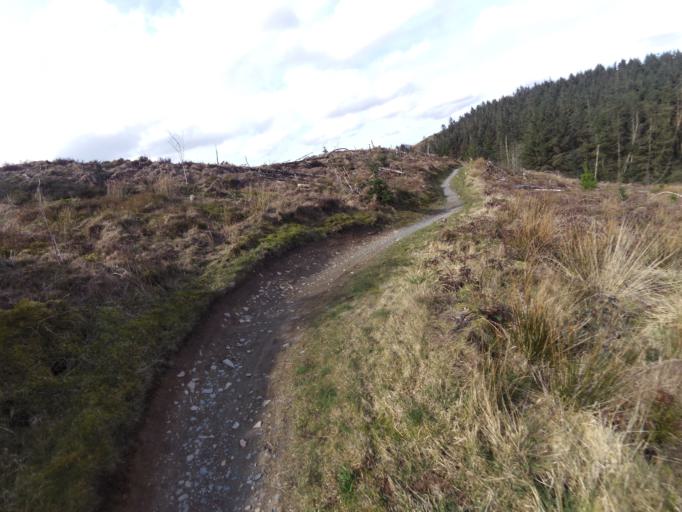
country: GB
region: Wales
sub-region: County of Ceredigion
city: Bow Street
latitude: 52.4235
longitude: -3.8838
